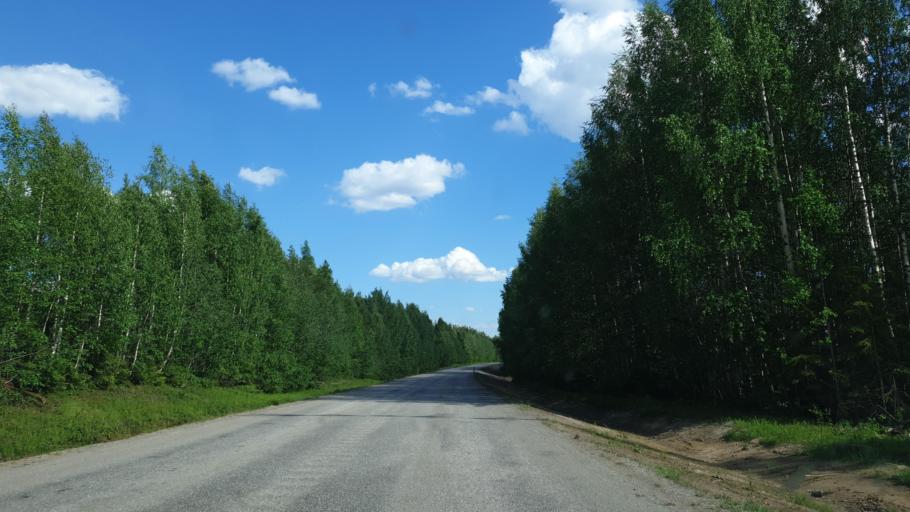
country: SE
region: Norrbotten
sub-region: Alvsbyns Kommun
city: AElvsbyn
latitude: 65.8327
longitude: 20.5372
